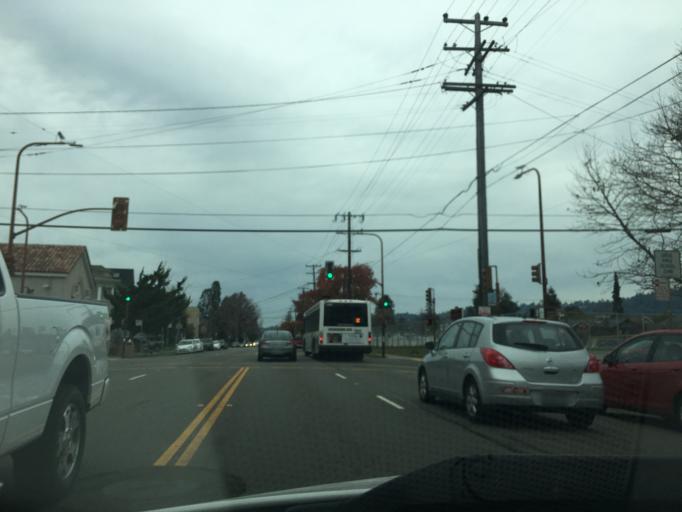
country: US
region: California
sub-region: Alameda County
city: Berkeley
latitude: 37.8593
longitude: -122.2716
